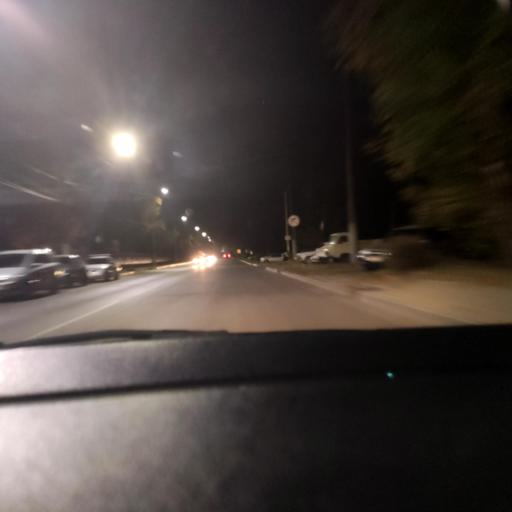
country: RU
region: Voronezj
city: Pridonskoy
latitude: 51.6514
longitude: 39.1006
